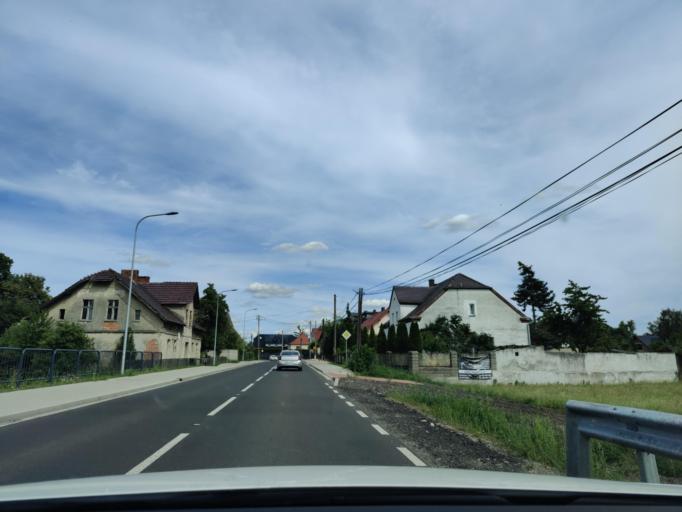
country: PL
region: Opole Voivodeship
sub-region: Powiat krapkowicki
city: Strzeleczki
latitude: 50.4407
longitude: 17.7966
